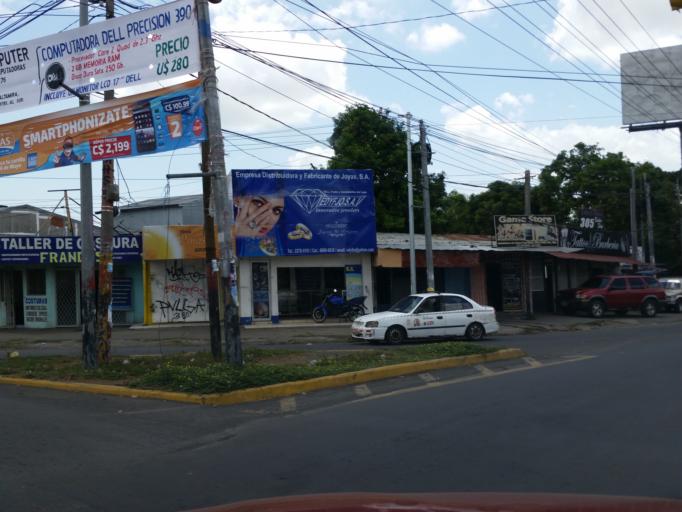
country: NI
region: Managua
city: Managua
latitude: 12.1169
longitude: -86.2513
